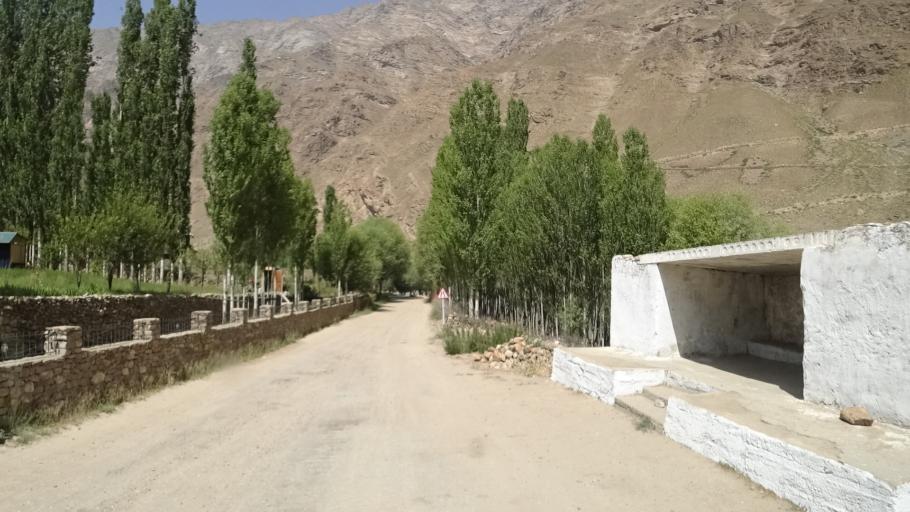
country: TJ
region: Gorno-Badakhshan
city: Khorugh
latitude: 37.1818
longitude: 71.4540
